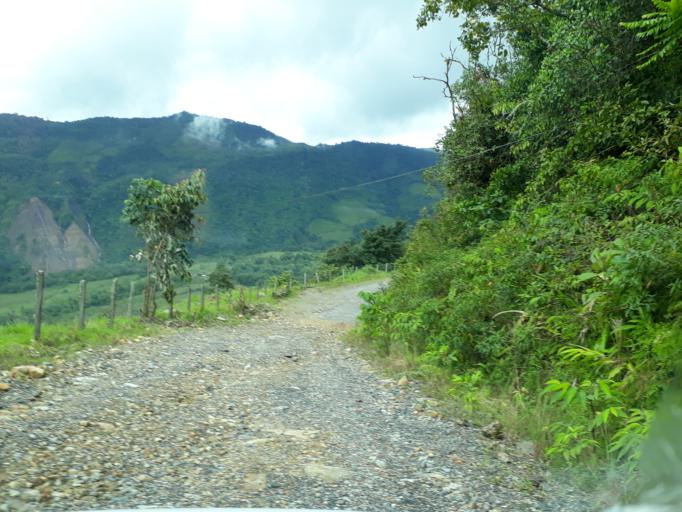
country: CO
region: Cundinamarca
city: Gachala
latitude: 4.7118
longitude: -73.3702
